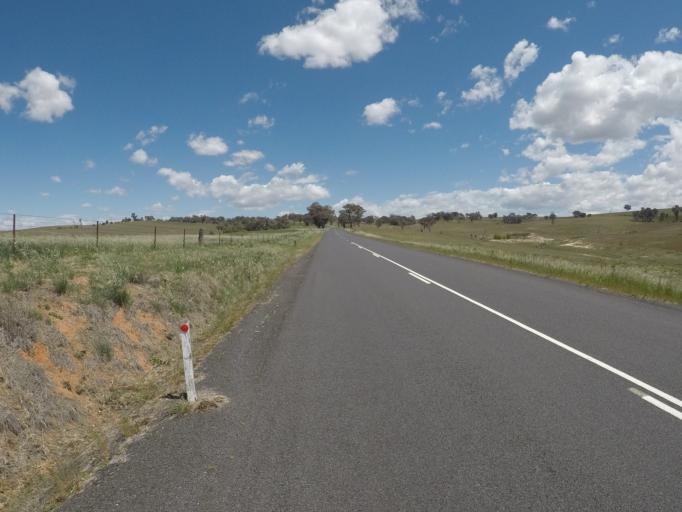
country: AU
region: New South Wales
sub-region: Bathurst Regional
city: Perthville
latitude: -33.5249
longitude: 149.4823
